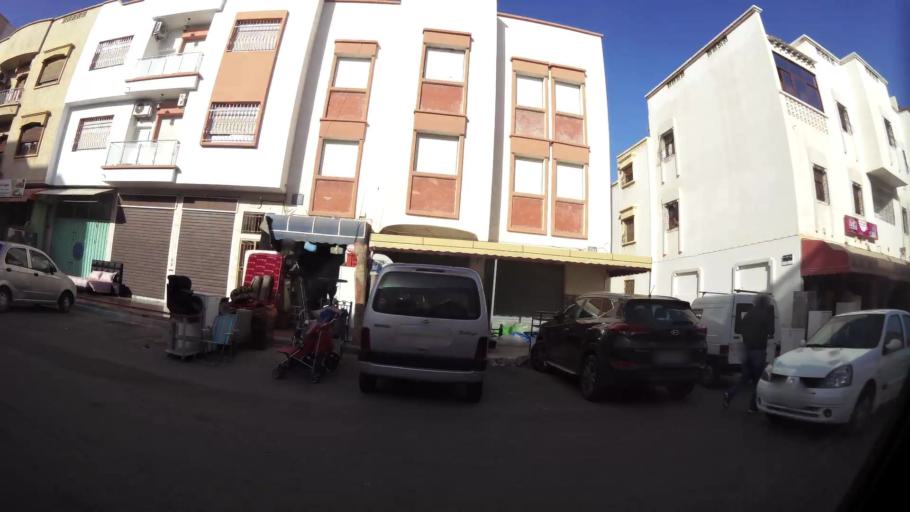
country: MA
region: Oued ed Dahab-Lagouira
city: Dakhla
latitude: 30.3970
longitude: -9.5462
